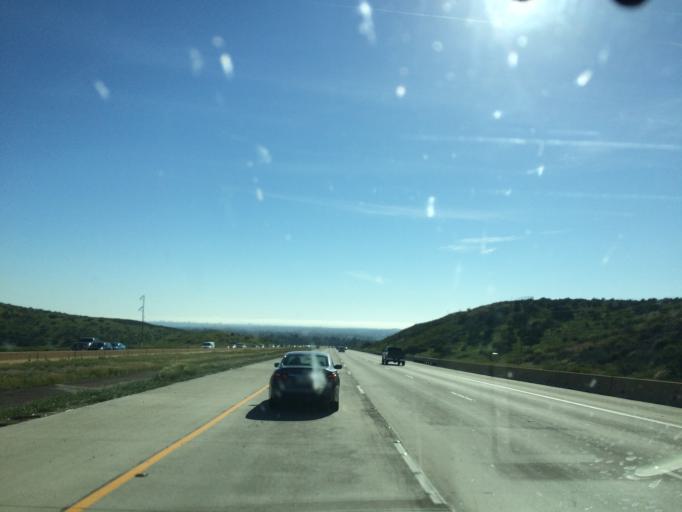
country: US
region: California
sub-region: San Diego County
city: La Mesa
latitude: 32.8515
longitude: -117.0722
